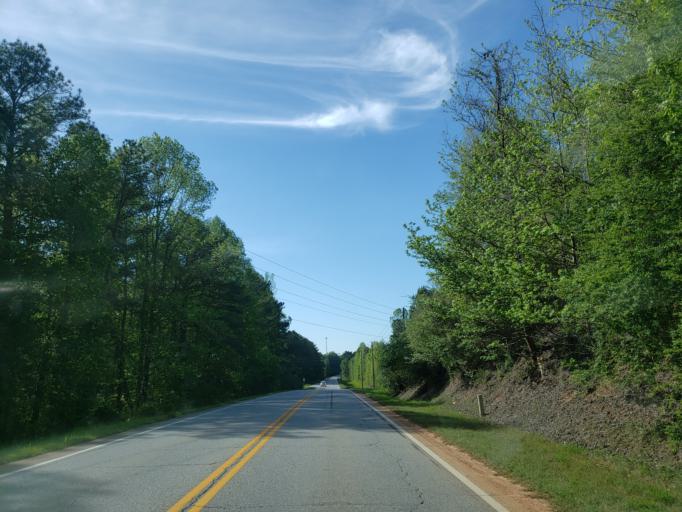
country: US
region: Georgia
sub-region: Haralson County
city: Tallapoosa
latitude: 33.6974
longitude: -85.2645
